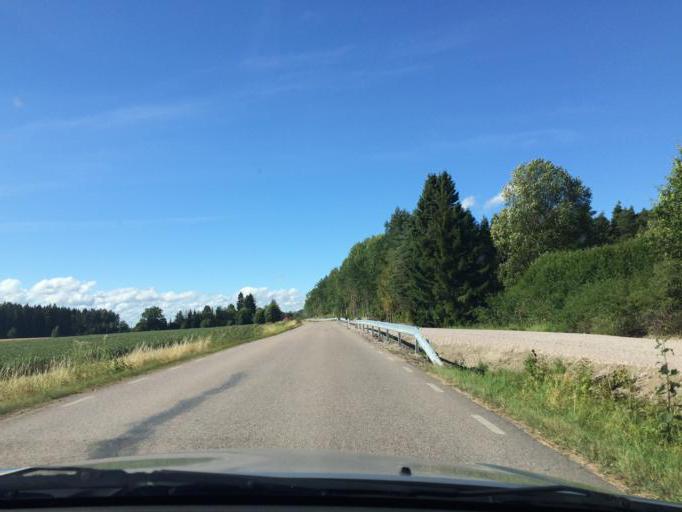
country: SE
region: Vaestmanland
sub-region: Vasteras
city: Vasteras
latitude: 59.5684
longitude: 16.4844
